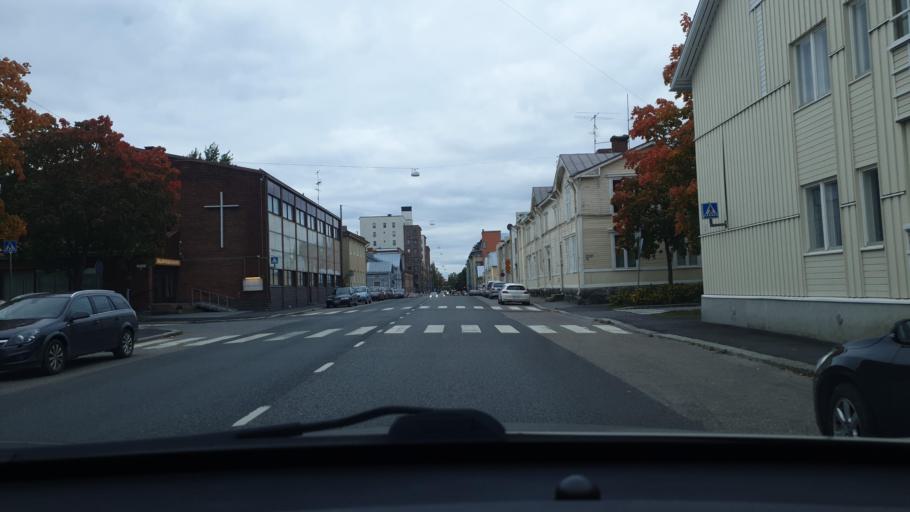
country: FI
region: Ostrobothnia
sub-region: Vaasa
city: Vaasa
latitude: 63.0929
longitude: 21.6249
